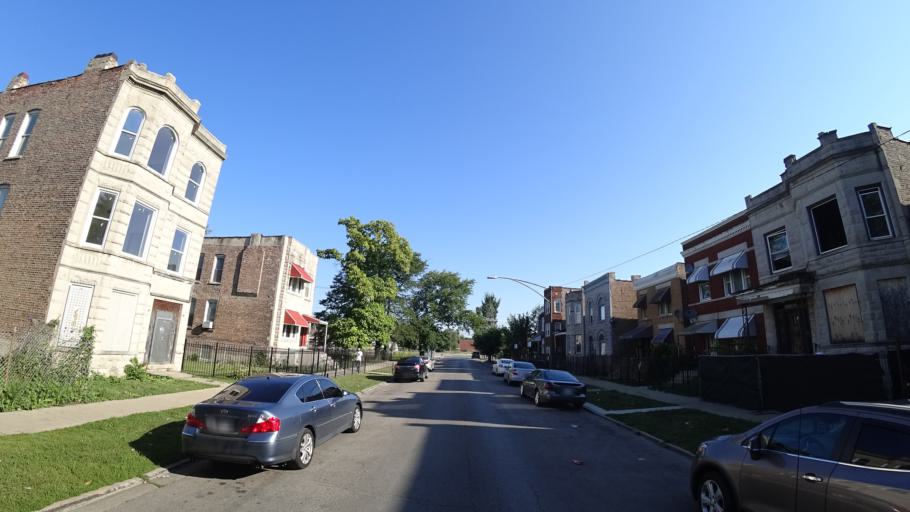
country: US
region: Illinois
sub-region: Cook County
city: Cicero
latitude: 41.8547
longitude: -87.7113
